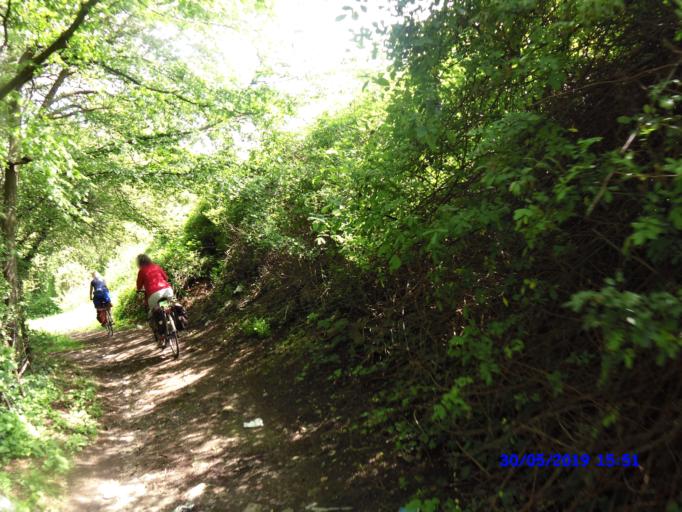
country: BE
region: Wallonia
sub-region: Province du Hainaut
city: Courcelles
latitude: 50.4051
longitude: 4.3635
